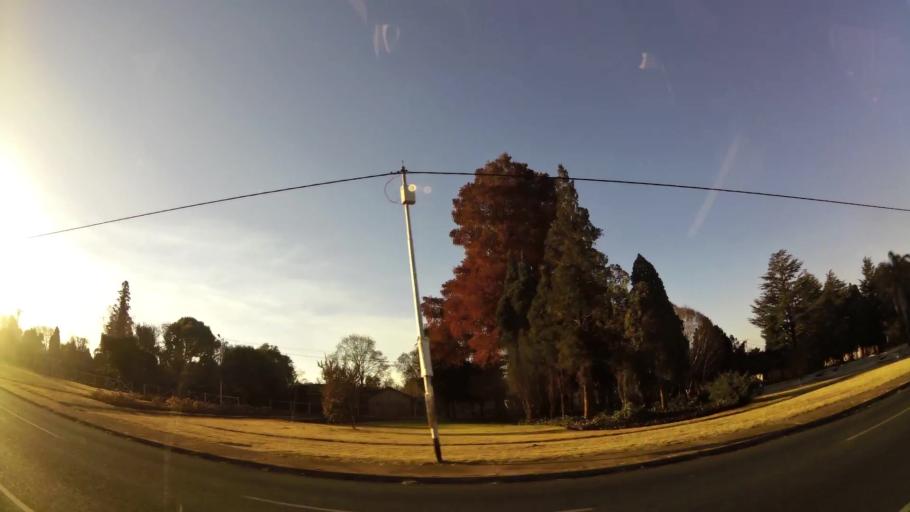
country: ZA
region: Gauteng
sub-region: City of Johannesburg Metropolitan Municipality
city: Roodepoort
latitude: -26.1689
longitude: 27.9012
